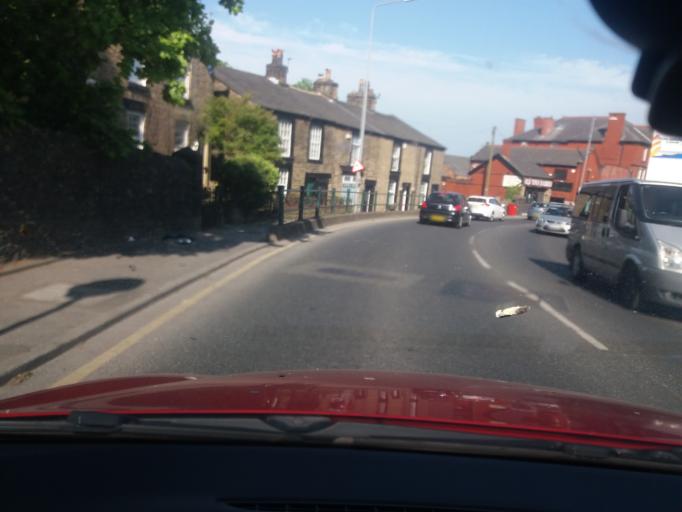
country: GB
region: England
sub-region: Borough of Bolton
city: Horwich
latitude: 53.5992
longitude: -2.5449
